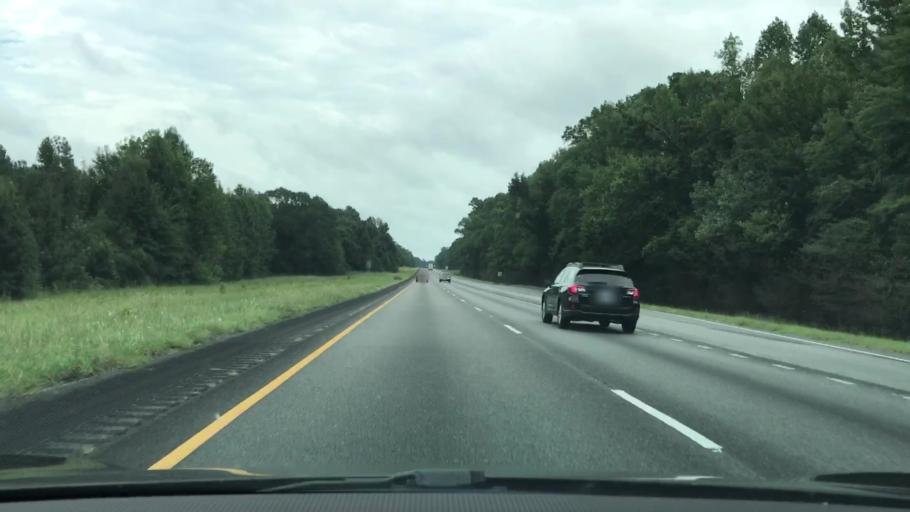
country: US
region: Alabama
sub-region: Elmore County
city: Tallassee
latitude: 32.4313
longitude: -85.8887
